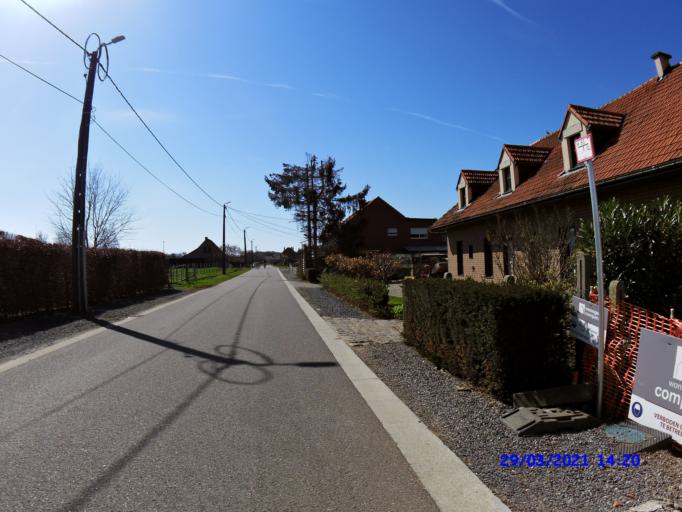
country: BE
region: Flanders
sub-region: Provincie Vlaams-Brabant
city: Bekkevoort
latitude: 50.9409
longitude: 4.9419
